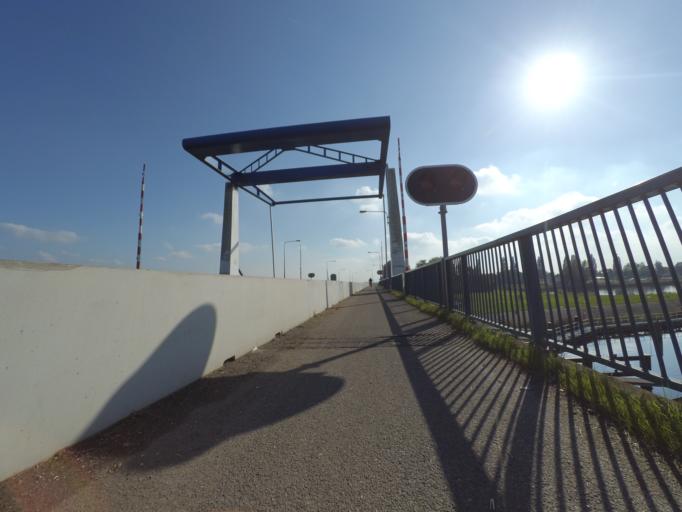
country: NL
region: Gelderland
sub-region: Gemeente Nijkerk
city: Nijkerk
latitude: 52.2624
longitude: 5.4709
